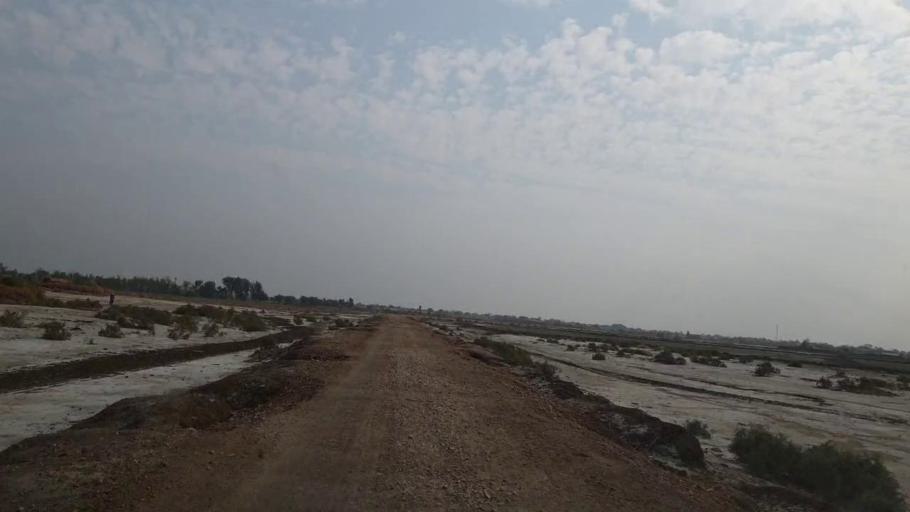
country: PK
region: Sindh
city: Mirpur Khas
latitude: 25.5562
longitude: 69.1581
